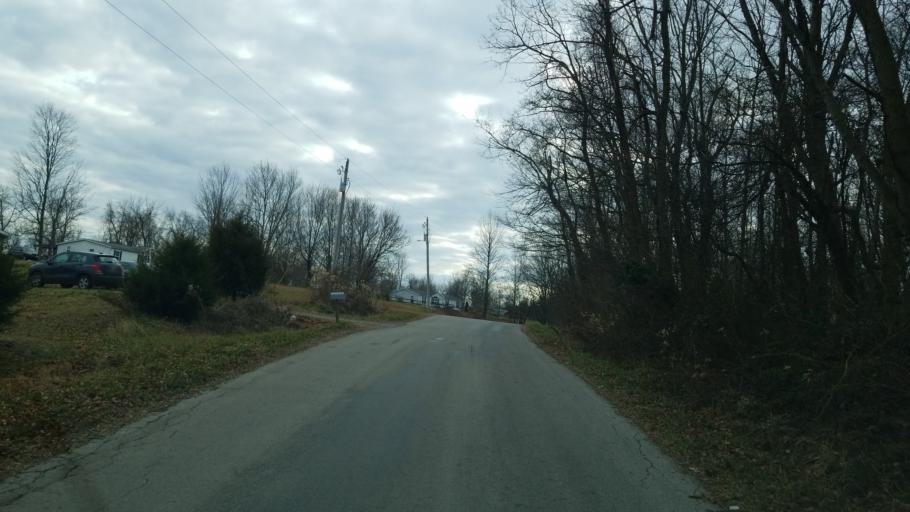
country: US
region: Ohio
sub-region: Highland County
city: Greenfield
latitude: 39.1832
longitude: -83.2662
